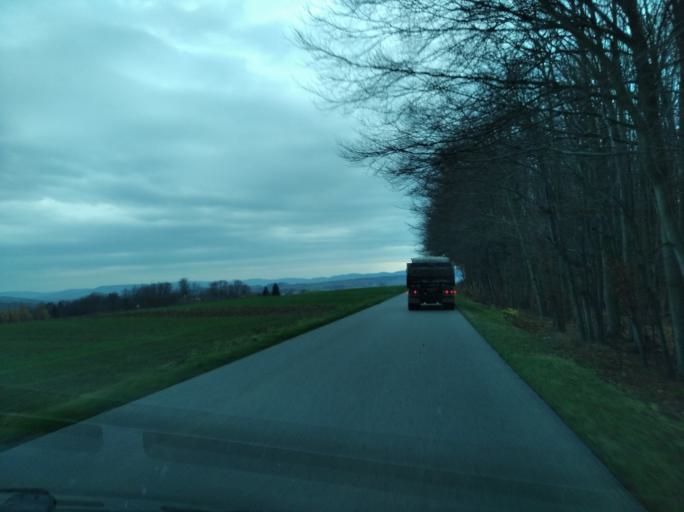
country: PL
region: Subcarpathian Voivodeship
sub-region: Powiat ropczycko-sedziszowski
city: Zagorzyce
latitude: 49.9439
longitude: 21.6936
